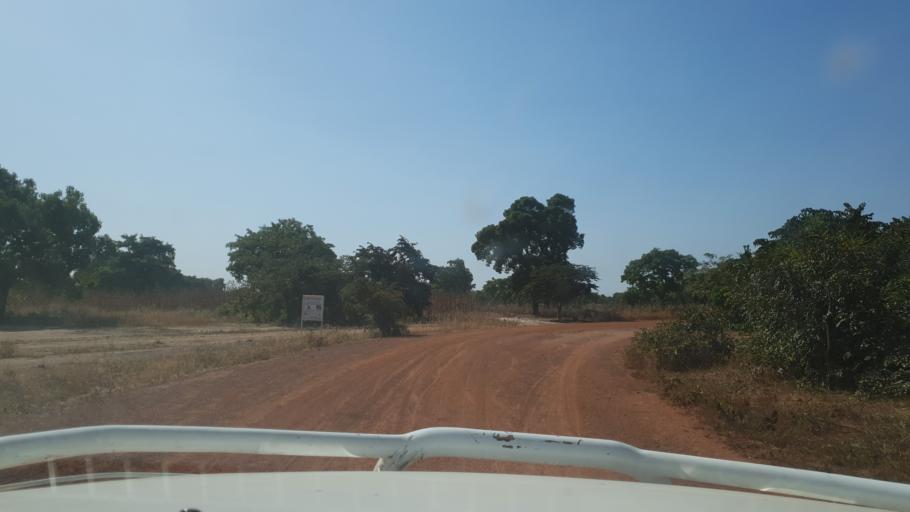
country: ML
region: Sikasso
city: Kolondieba
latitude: 11.5960
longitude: -6.6637
